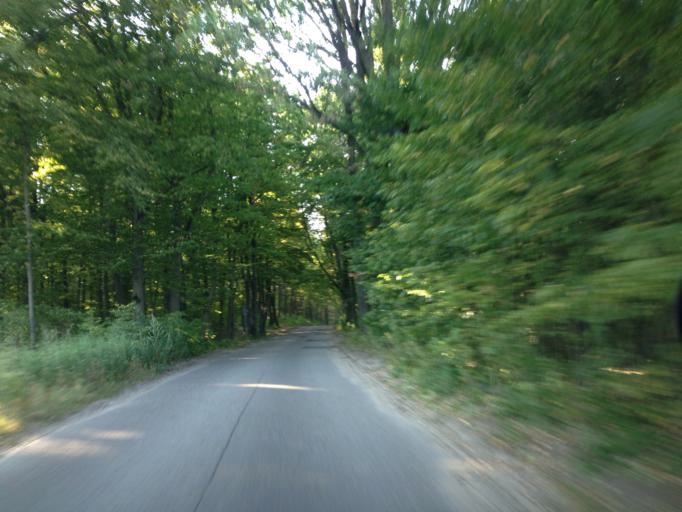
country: PL
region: Warmian-Masurian Voivodeship
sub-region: Powiat dzialdowski
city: Lidzbark
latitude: 53.2420
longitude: 19.7504
